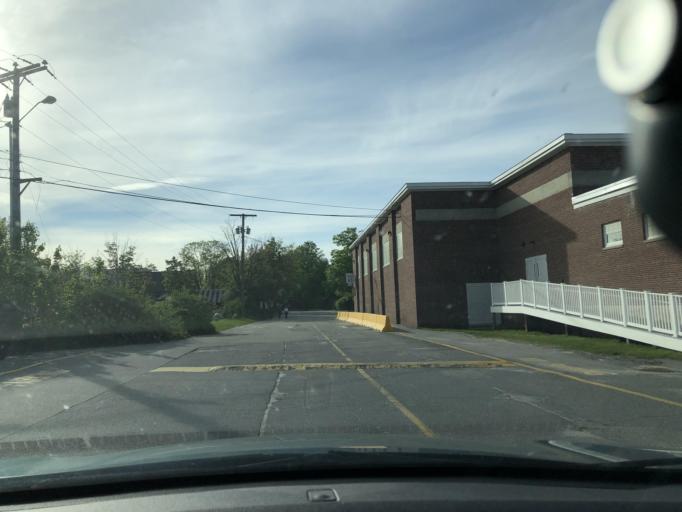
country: US
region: New Hampshire
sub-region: Merrimack County
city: New London
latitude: 43.4163
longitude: -71.9864
